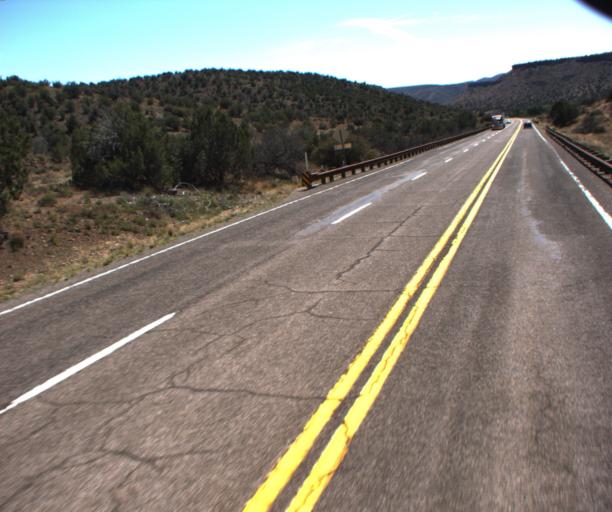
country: US
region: Arizona
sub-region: Mohave County
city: Peach Springs
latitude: 35.4463
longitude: -113.6388
